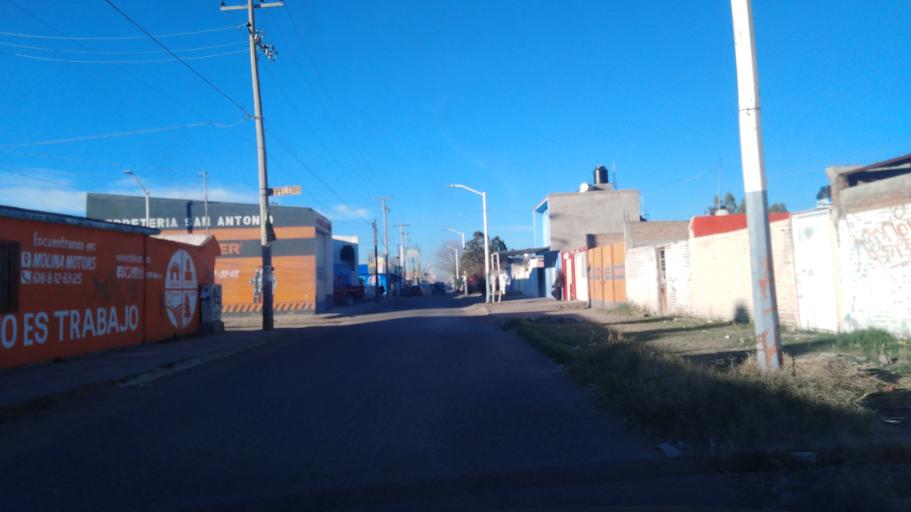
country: MX
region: Durango
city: Victoria de Durango
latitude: 24.0564
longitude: -104.6021
